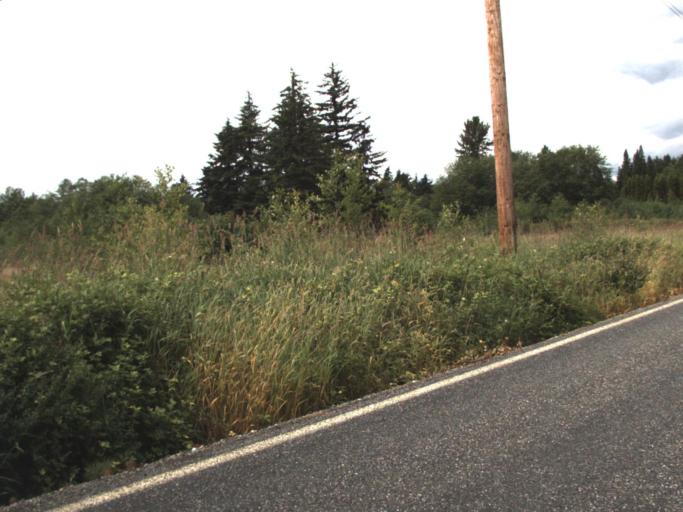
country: US
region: Washington
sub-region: Whatcom County
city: Birch Bay
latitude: 48.8943
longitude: -122.7266
